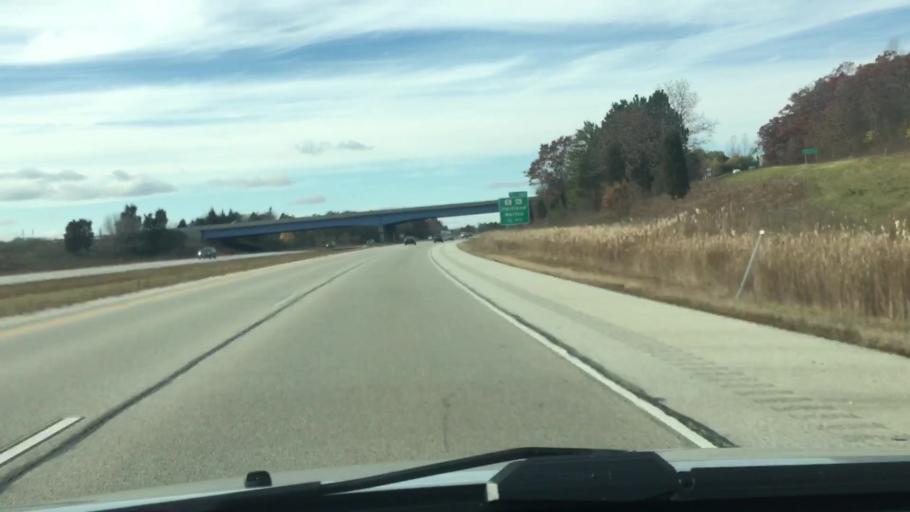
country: US
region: Wisconsin
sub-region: Waukesha County
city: Hartland
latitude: 43.1038
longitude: -88.3108
